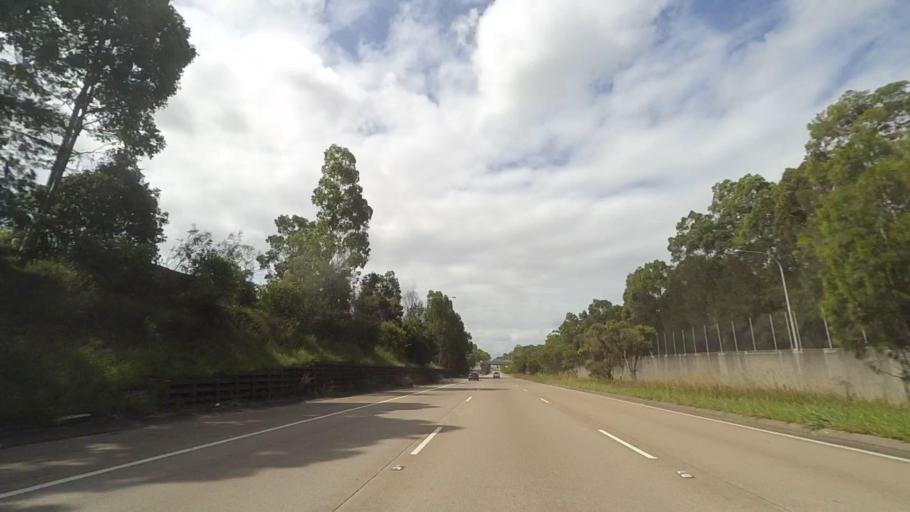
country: AU
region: New South Wales
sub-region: Newcastle
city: North Lambton
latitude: -32.9009
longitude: 151.6938
